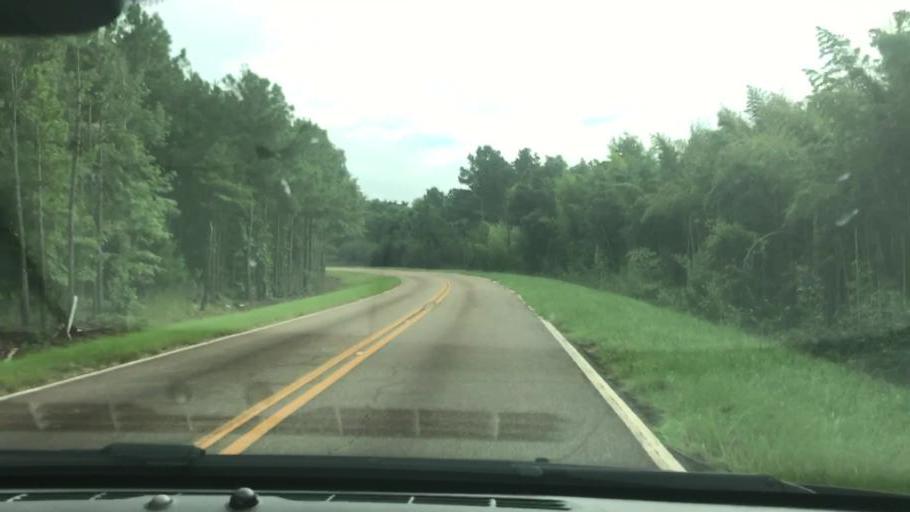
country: US
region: Georgia
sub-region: Stewart County
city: Lumpkin
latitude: 32.0494
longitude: -84.9041
